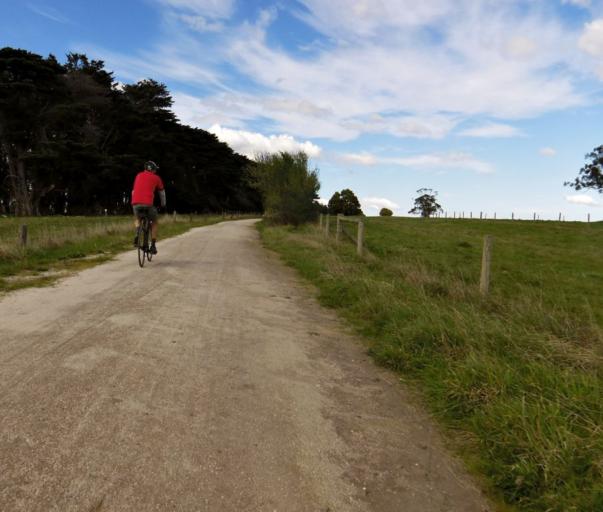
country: AU
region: Victoria
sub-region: Bass Coast
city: North Wonthaggi
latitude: -38.5248
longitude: 145.9448
